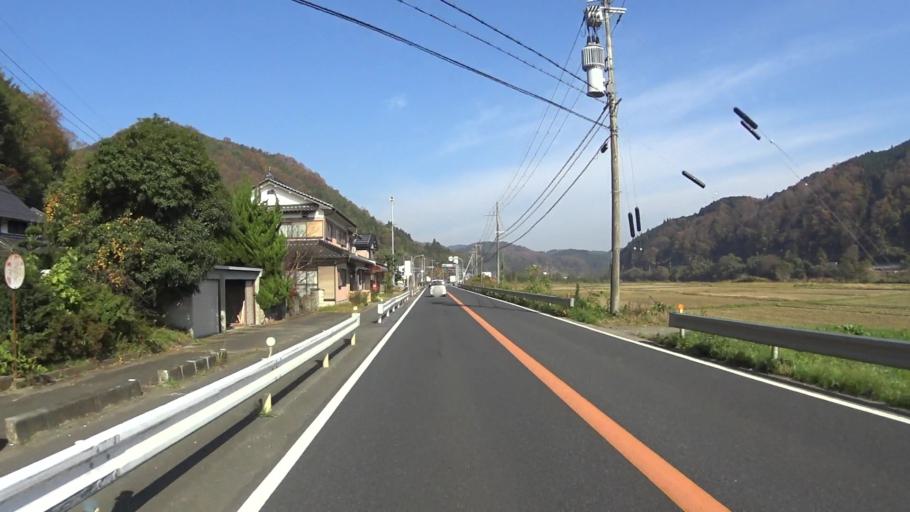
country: JP
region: Kyoto
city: Fukuchiyama
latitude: 35.3559
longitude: 135.1125
